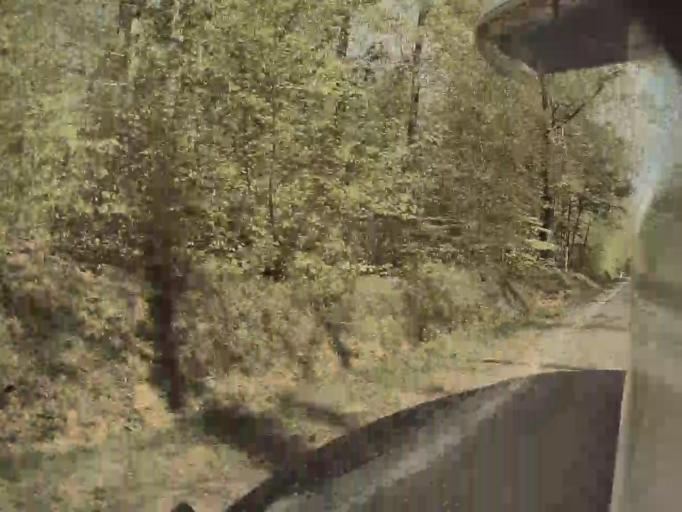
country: BE
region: Wallonia
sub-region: Province du Luxembourg
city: Tellin
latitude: 50.0389
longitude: 5.2082
